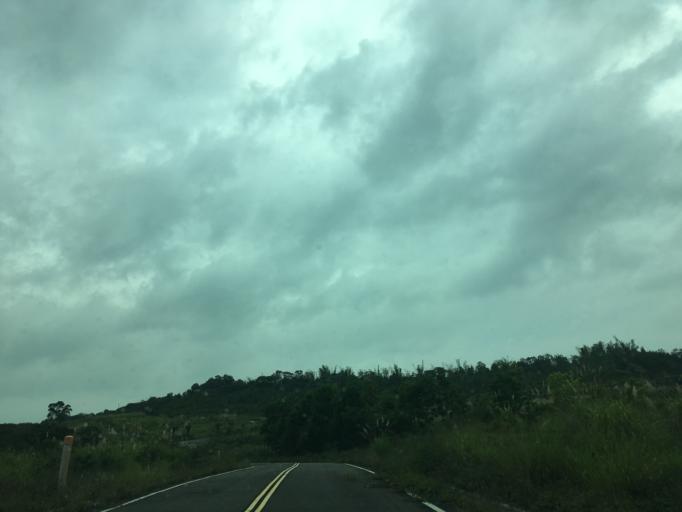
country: TW
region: Taiwan
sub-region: Taichung City
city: Taichung
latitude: 24.0597
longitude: 120.7290
